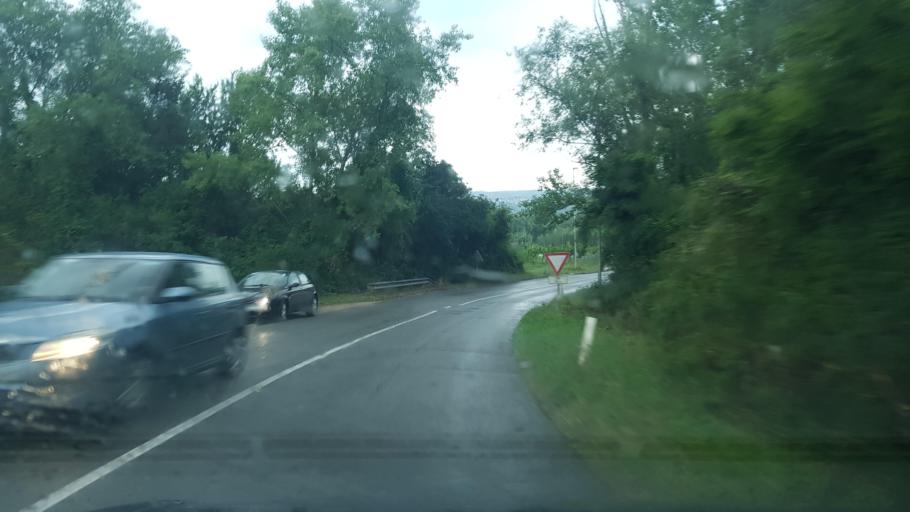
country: SI
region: Koper-Capodistria
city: Hrvatini
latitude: 45.5694
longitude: 13.7704
